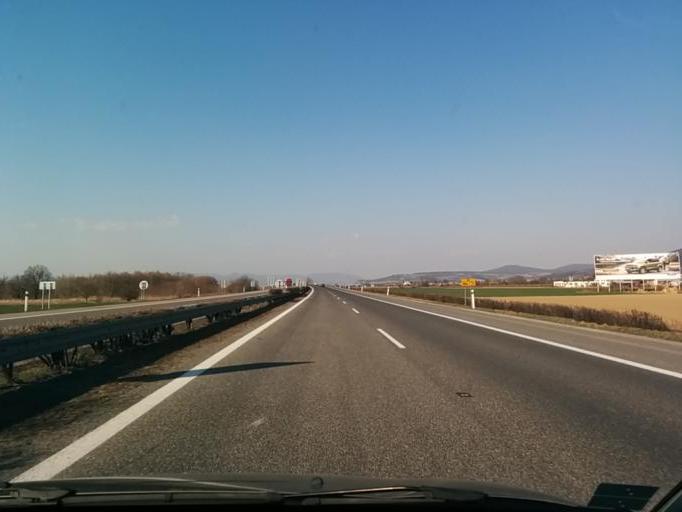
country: SK
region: Trenciansky
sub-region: Okres Nove Mesto nad Vahom
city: Nove Mesto nad Vahom
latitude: 48.7138
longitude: 17.8737
